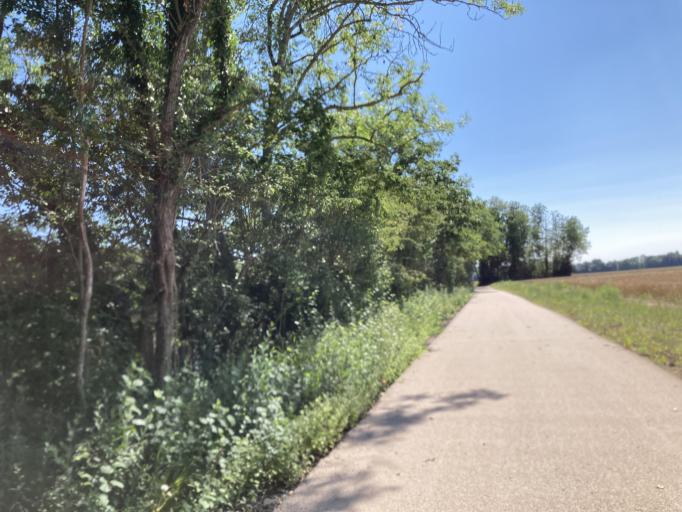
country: FR
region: Bourgogne
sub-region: Departement de l'Yonne
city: Laroche-Saint-Cydroine
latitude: 47.9661
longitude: 3.4470
